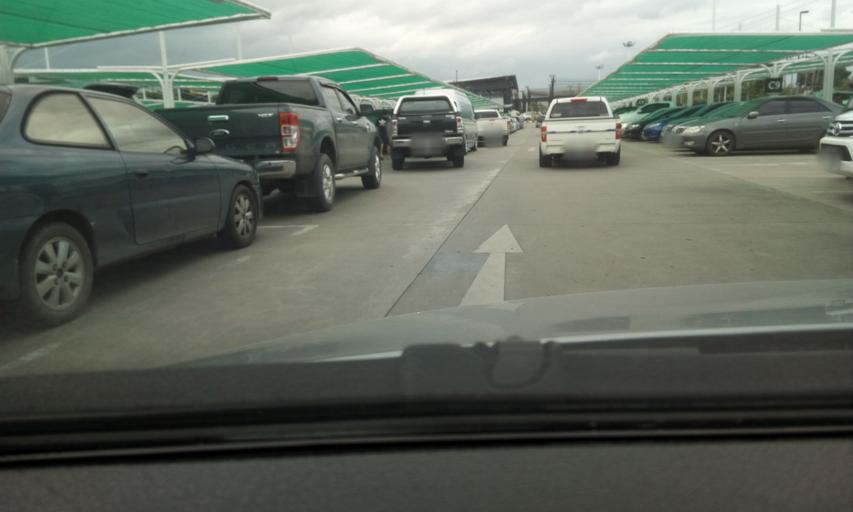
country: TH
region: Phra Nakhon Si Ayutthaya
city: Ban Bang Kadi Pathum Thani
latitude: 13.9905
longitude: 100.6201
